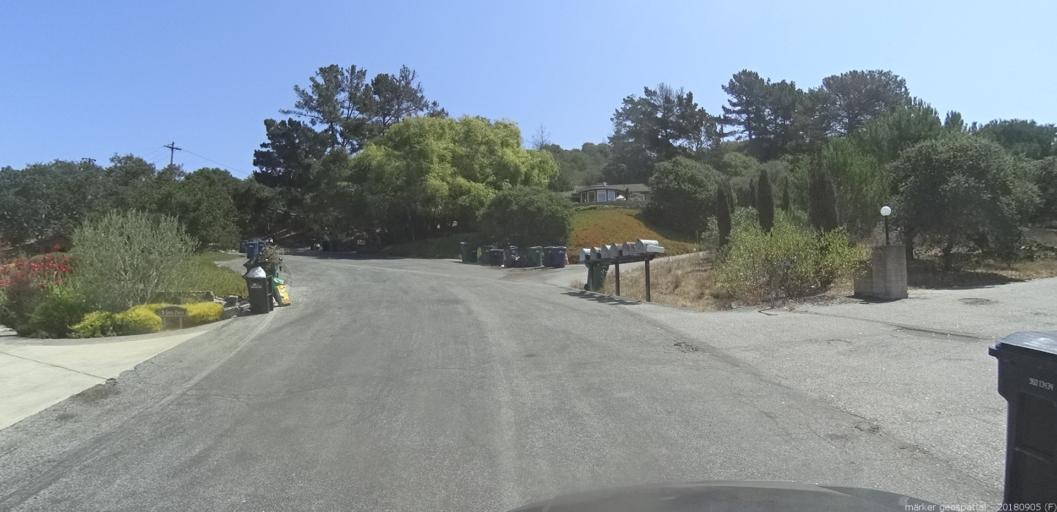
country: US
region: California
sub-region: Monterey County
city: Carmel Valley Village
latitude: 36.5678
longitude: -121.7535
